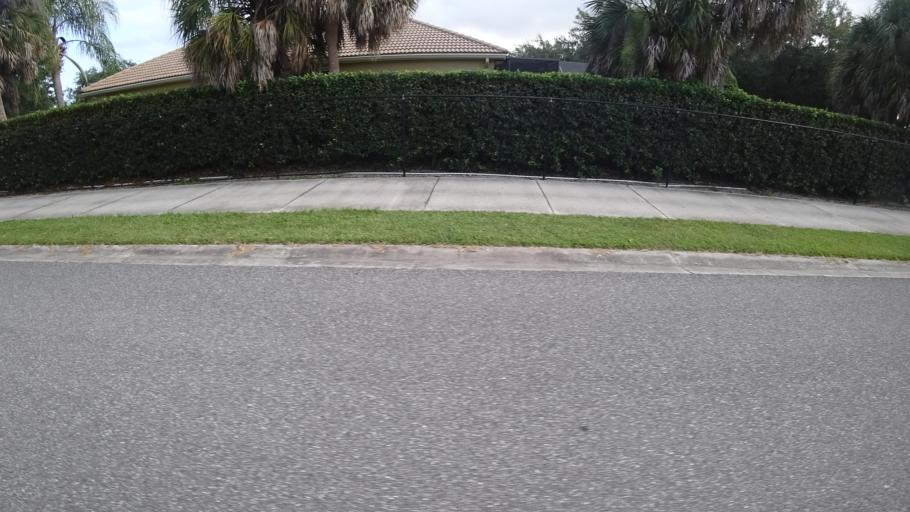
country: US
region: Florida
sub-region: Sarasota County
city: Desoto Lakes
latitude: 27.4108
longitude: -82.4977
